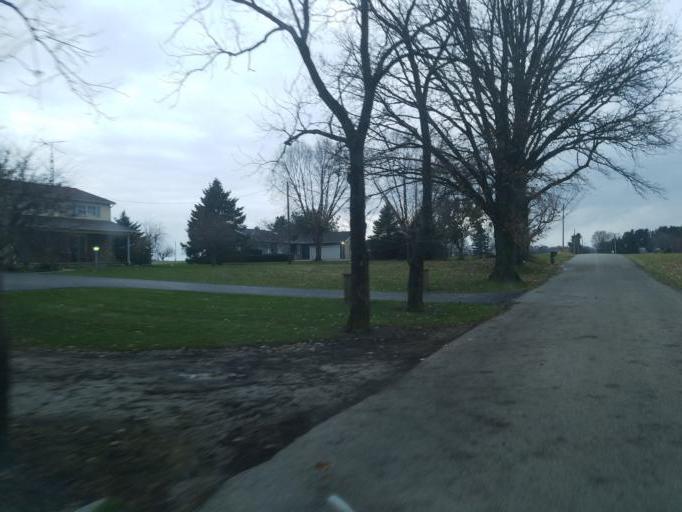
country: US
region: Ohio
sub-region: Morrow County
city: Mount Gilead
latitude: 40.5565
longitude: -82.7964
